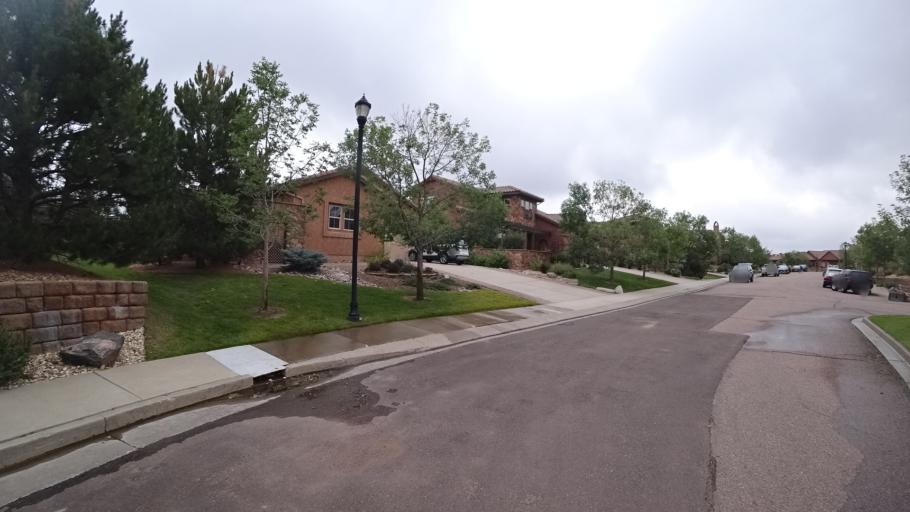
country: US
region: Colorado
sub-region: El Paso County
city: Gleneagle
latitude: 39.0223
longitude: -104.7858
